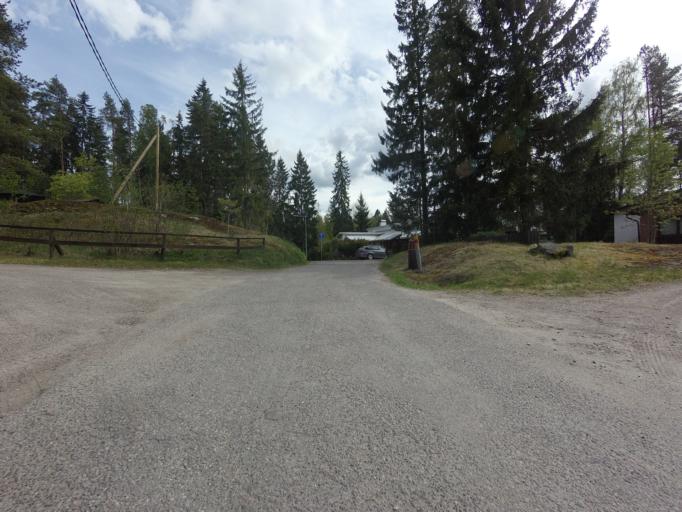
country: FI
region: Uusimaa
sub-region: Helsinki
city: Kauniainen
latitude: 60.1869
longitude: 24.7218
